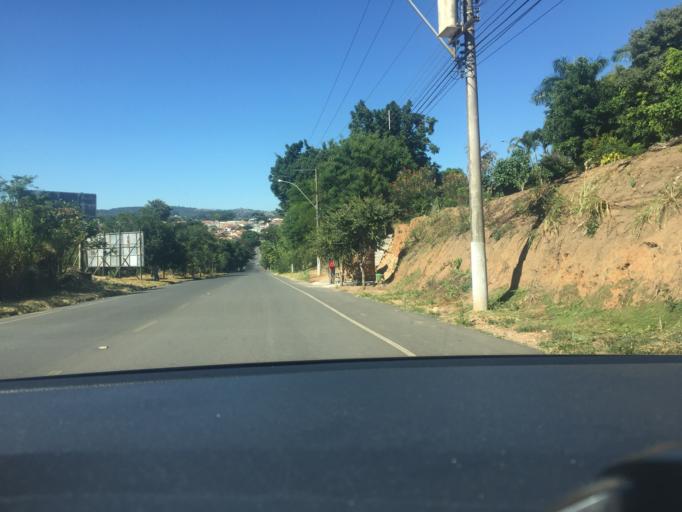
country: BR
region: Sao Paulo
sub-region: Santo Antonio Do Jardim
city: Espirito Santo do Pinhal
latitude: -22.1760
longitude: -46.7462
